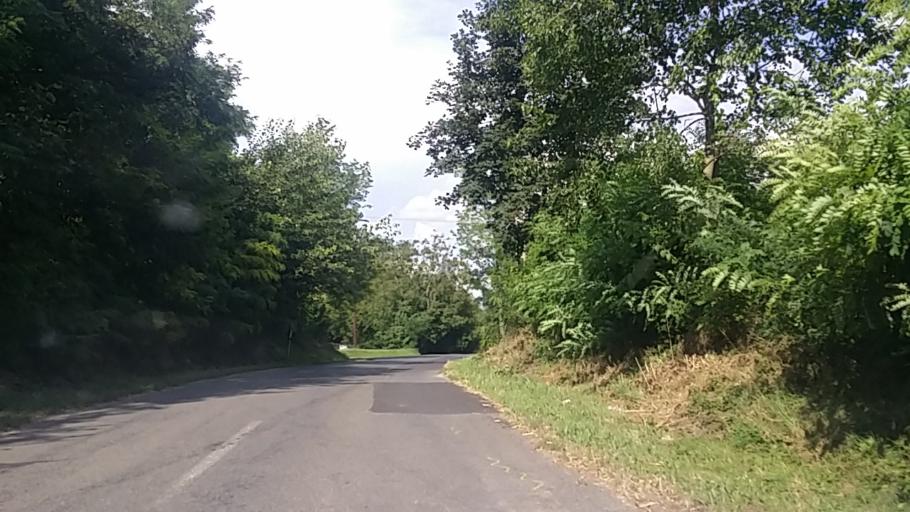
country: HU
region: Tolna
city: Gyonk
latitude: 46.5425
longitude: 18.4778
